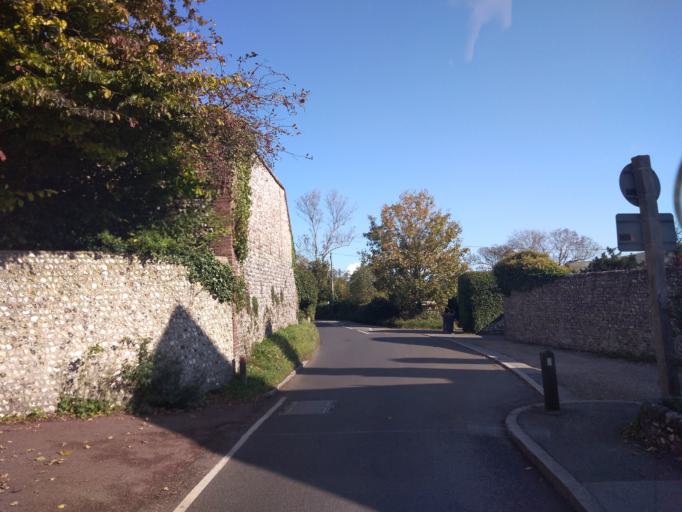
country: GB
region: England
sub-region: East Sussex
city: Seaford
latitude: 50.7973
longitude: 0.1522
